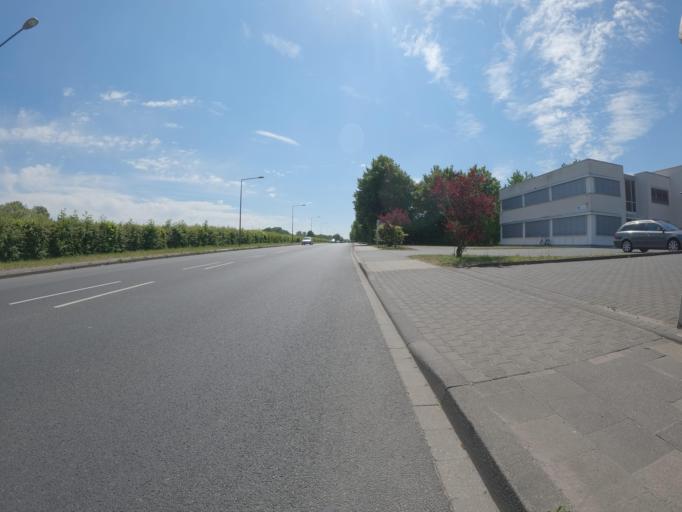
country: DE
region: North Rhine-Westphalia
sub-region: Regierungsbezirk Koln
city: Wurselen
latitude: 50.7653
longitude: 6.1627
